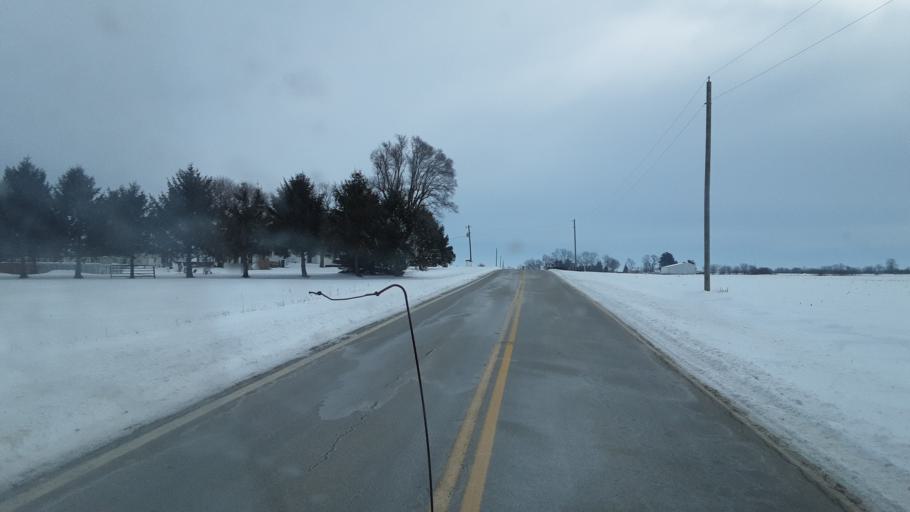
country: US
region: Ohio
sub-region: Madison County
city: Choctaw Lake
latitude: 40.0163
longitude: -83.5124
